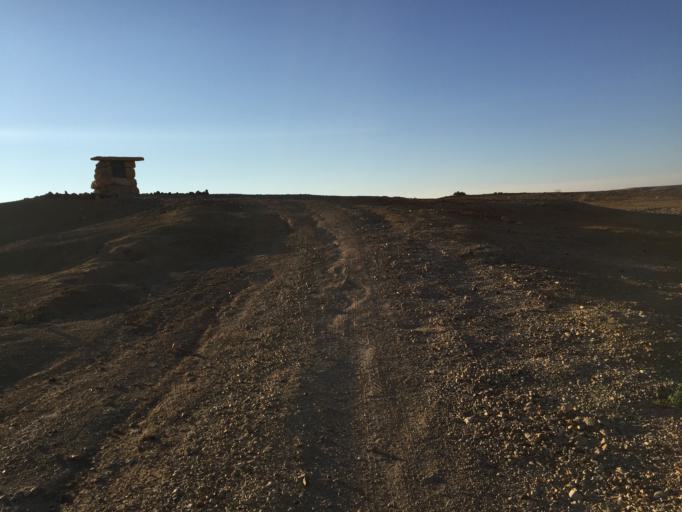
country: IL
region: Southern District
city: Mitzpe Ramon
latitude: 30.5289
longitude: 34.9203
